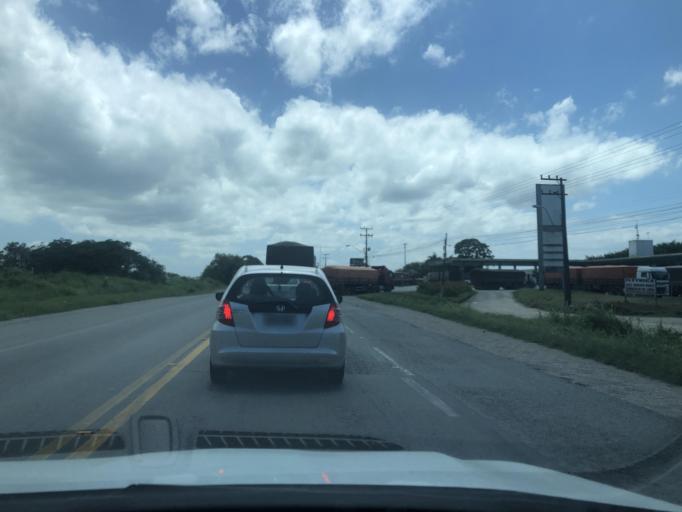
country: BR
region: Santa Catarina
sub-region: Sao Francisco Do Sul
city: Sao Francisco do Sul
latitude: -26.3711
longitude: -48.7046
